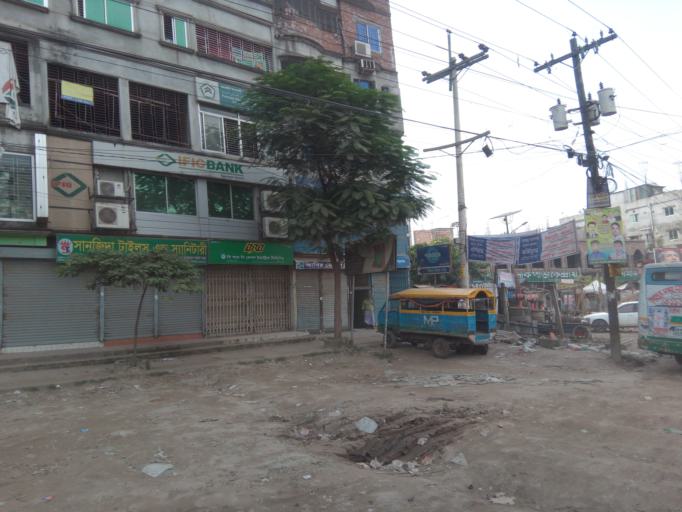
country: BD
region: Dhaka
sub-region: Dhaka
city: Dhaka
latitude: 23.6999
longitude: 90.3976
